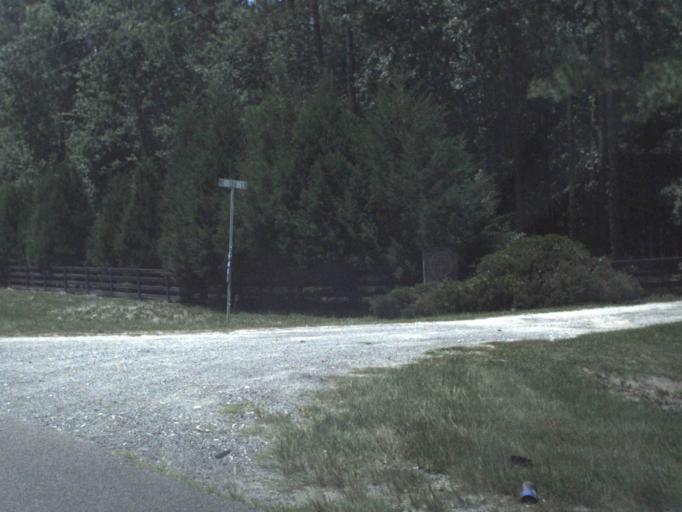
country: US
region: Florida
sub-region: Union County
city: Lake Butler
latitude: 30.0096
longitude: -82.2976
